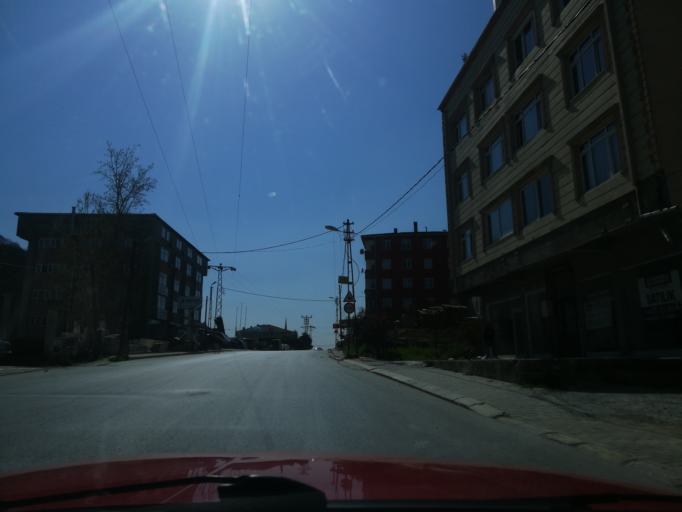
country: TR
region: Istanbul
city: Mahmut Sevket Pasa
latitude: 41.0985
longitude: 29.1518
